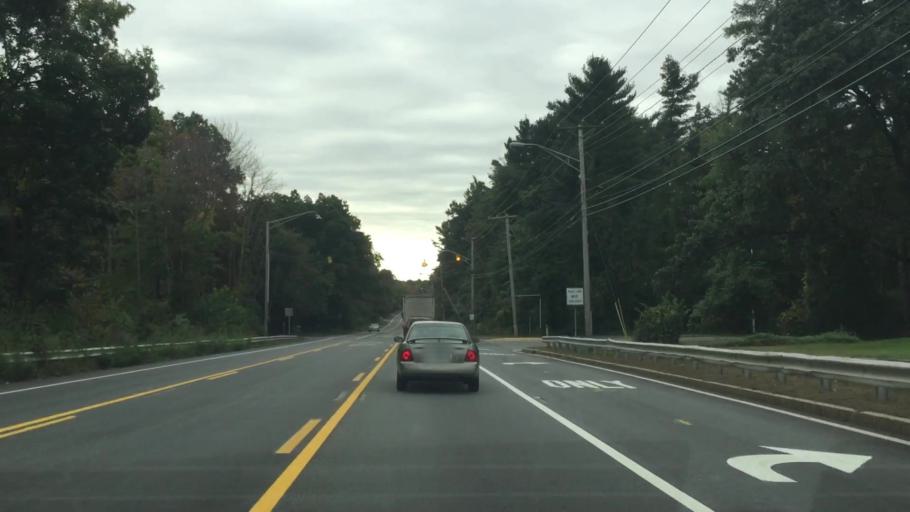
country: US
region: Massachusetts
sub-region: Essex County
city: Andover
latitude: 42.6538
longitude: -71.0991
